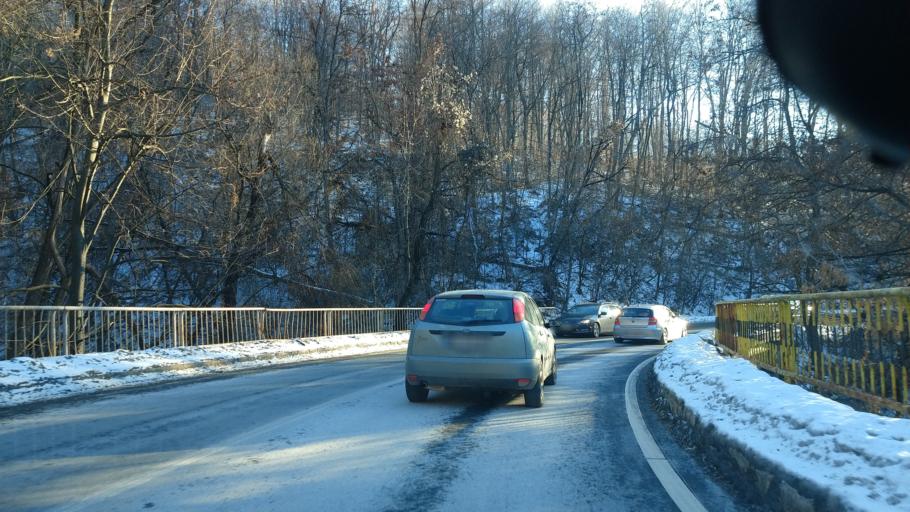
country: RO
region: Bacau
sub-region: Comuna Luizi-Calugara
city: Luizi-Calugara
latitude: 46.5424
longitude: 26.8211
